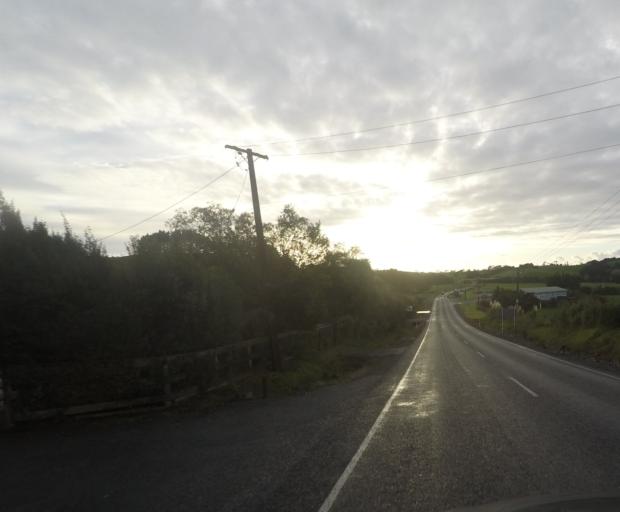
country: NZ
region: Auckland
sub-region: Auckland
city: Wellsford
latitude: -36.2215
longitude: 174.5767
